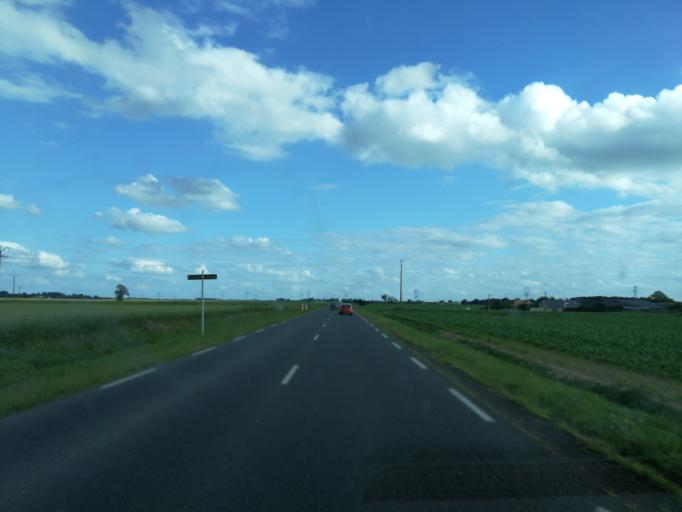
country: FR
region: Haute-Normandie
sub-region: Departement de l'Eure
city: Le Neubourg
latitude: 49.1037
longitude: 0.9157
